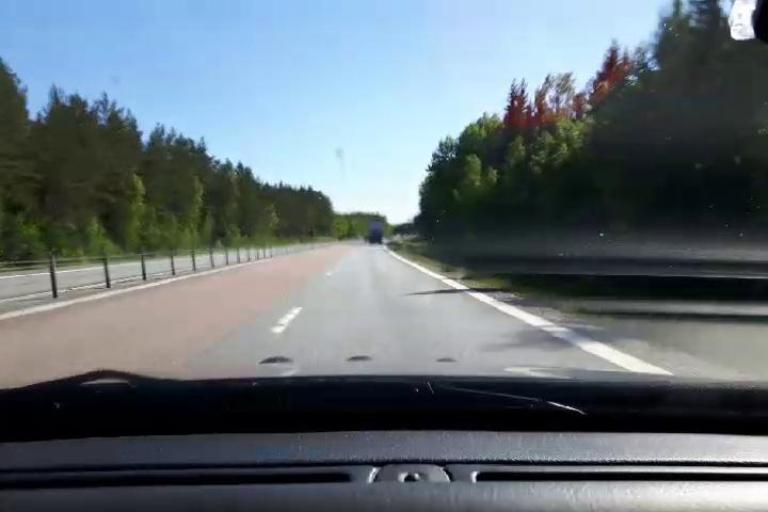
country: SE
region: Gaevleborg
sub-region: Gavle Kommun
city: Gavle
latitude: 60.7382
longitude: 17.0798
